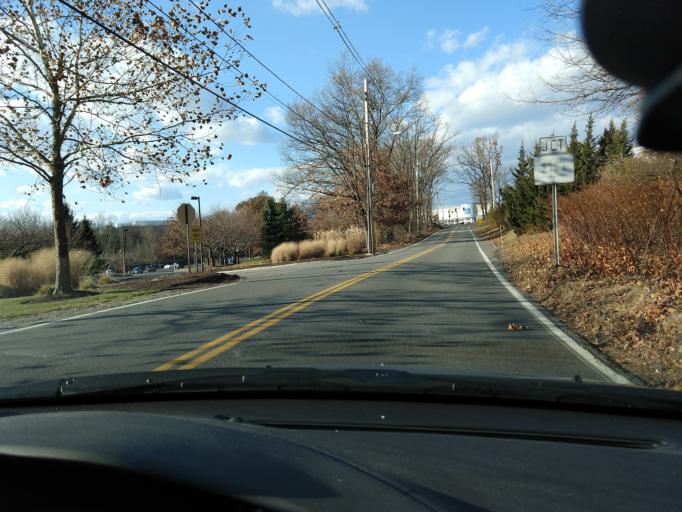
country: US
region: Massachusetts
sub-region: Middlesex County
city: Westford
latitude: 42.5536
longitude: -71.4401
